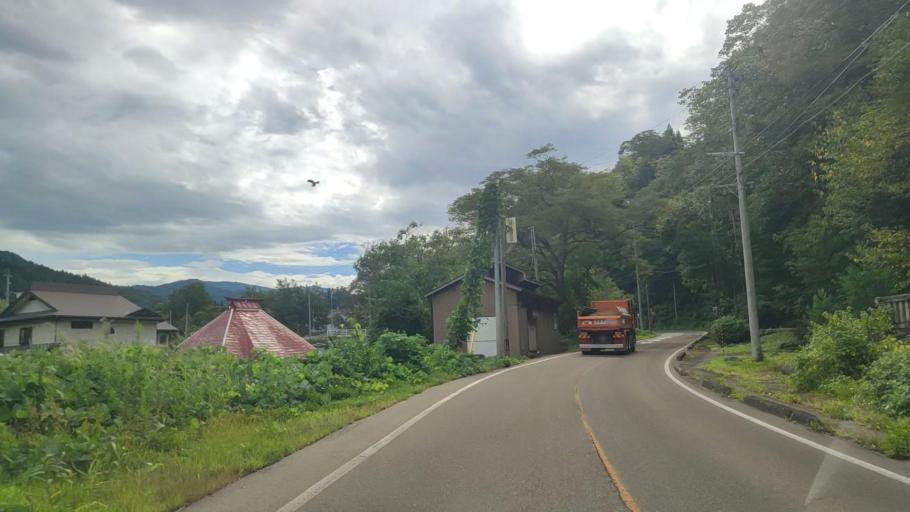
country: JP
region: Niigata
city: Arai
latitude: 36.9562
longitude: 138.2717
